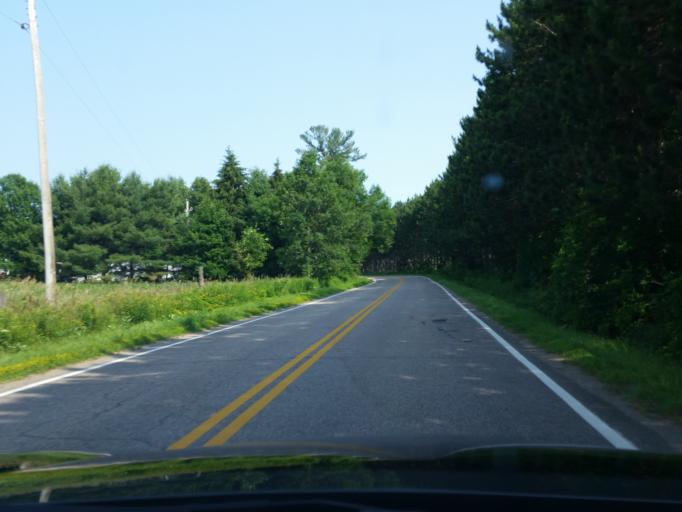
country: CA
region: Quebec
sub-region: Outaouais
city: Shawville
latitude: 45.5258
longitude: -76.4523
